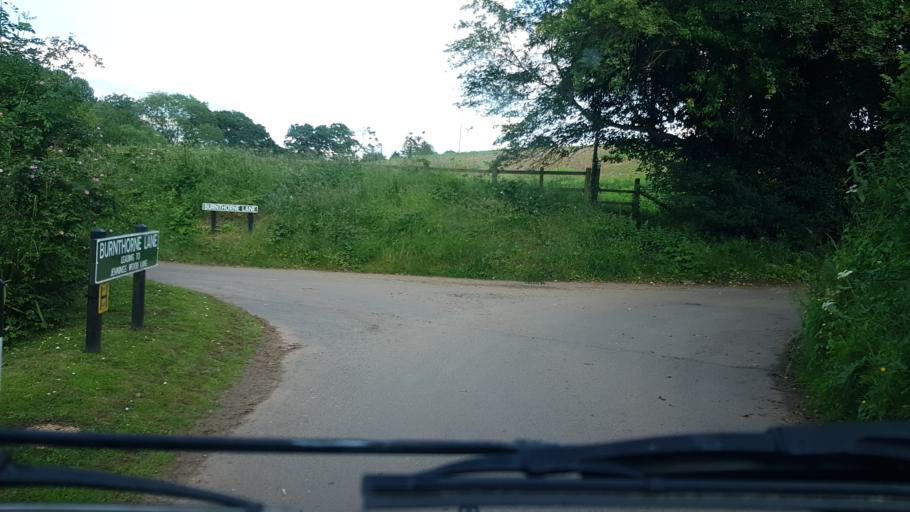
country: GB
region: England
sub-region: Worcestershire
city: Stourport-on-Severn
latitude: 52.3265
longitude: -2.3105
